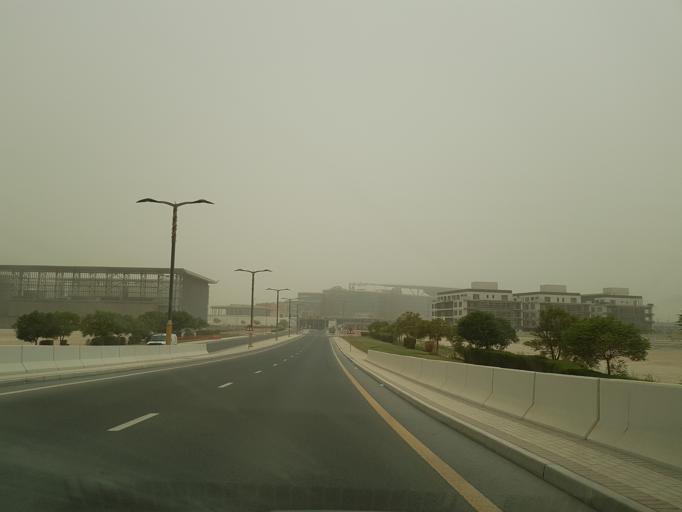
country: AE
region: Dubai
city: Dubai
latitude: 25.1655
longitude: 55.3031
